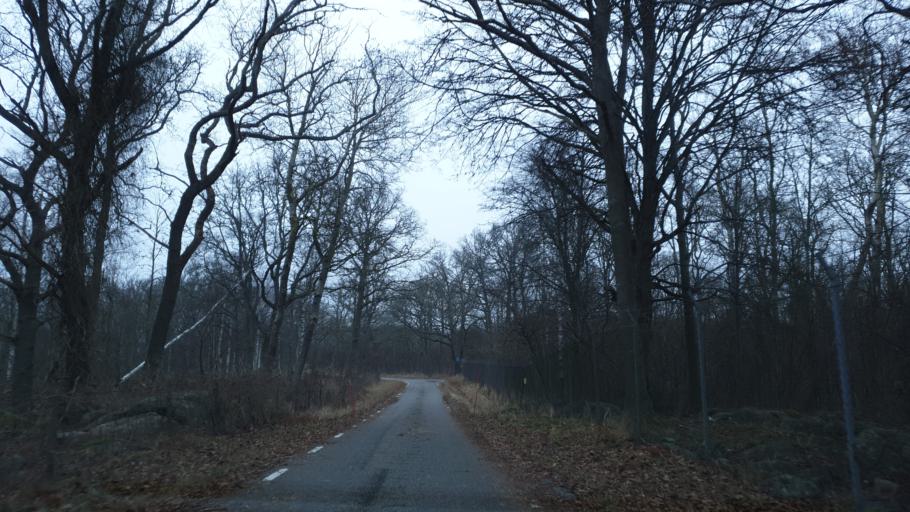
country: SE
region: Blekinge
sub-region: Karlskrona Kommun
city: Karlskrona
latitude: 56.1027
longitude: 15.6059
